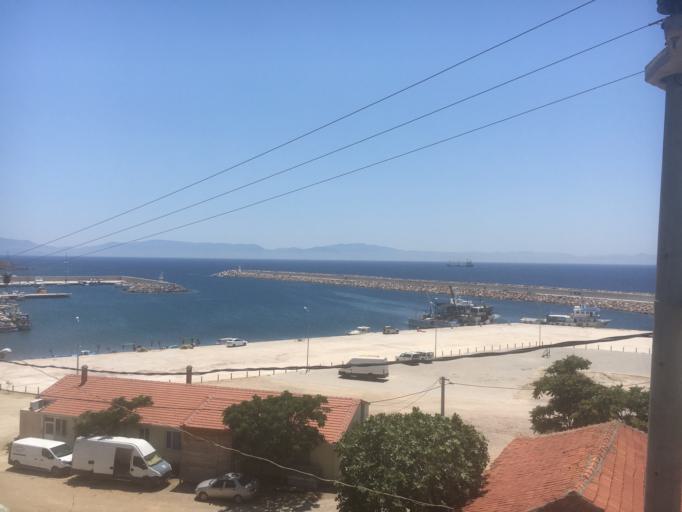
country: TR
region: Canakkale
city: Gulpinar
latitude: 39.4789
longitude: 26.0651
